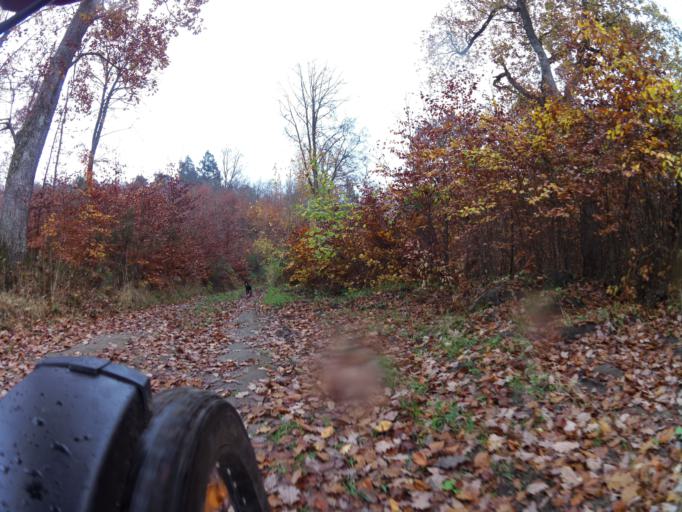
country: PL
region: Pomeranian Voivodeship
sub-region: Powiat wejherowski
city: Gniewino
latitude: 54.7554
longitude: 18.0819
